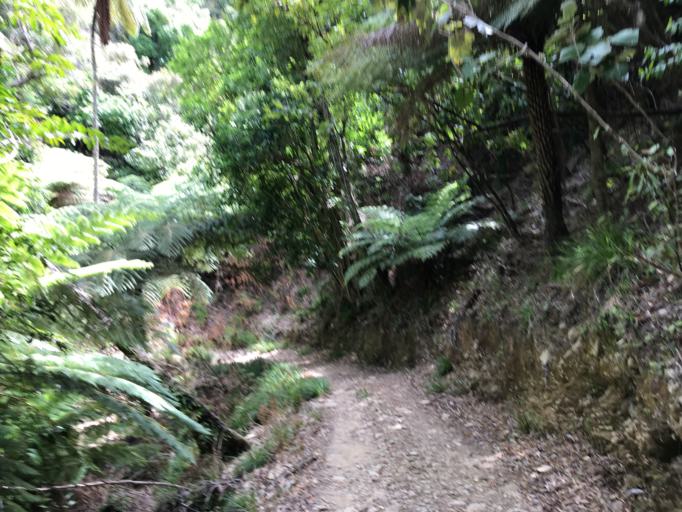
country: NZ
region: Marlborough
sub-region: Marlborough District
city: Picton
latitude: -41.1211
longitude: 174.1920
